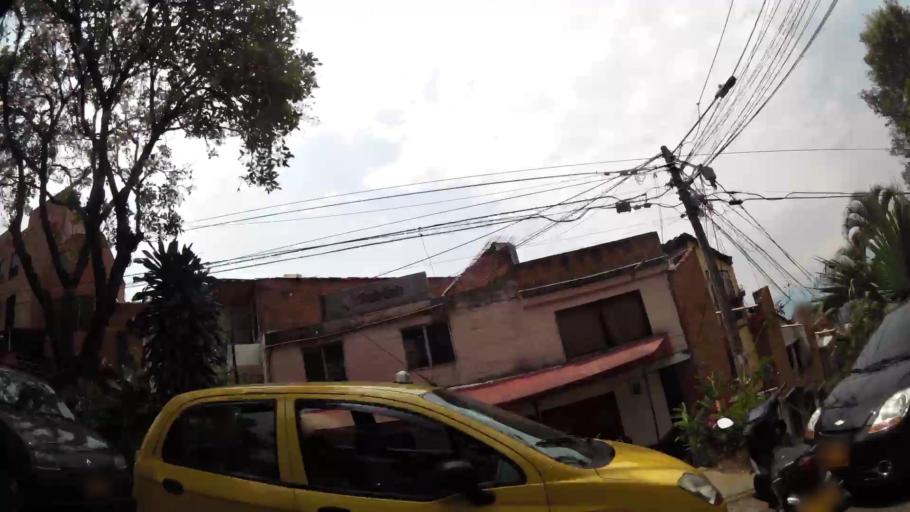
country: CO
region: Antioquia
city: Medellin
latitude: 6.2289
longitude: -75.5440
